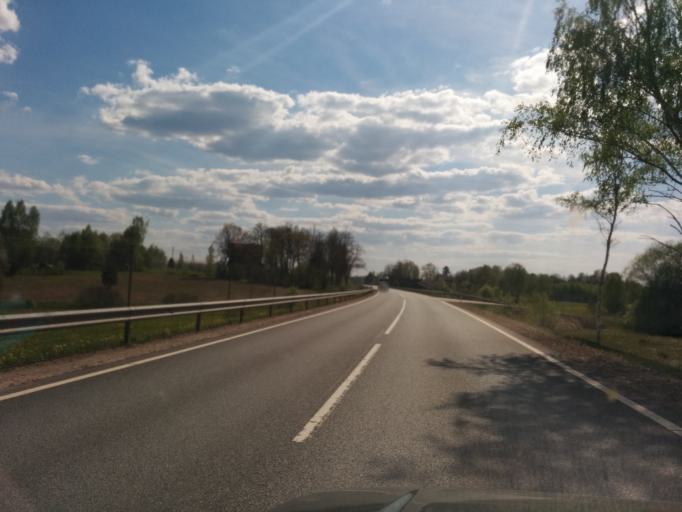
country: LV
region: Krimulda
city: Ragana
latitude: 57.1886
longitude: 24.7266
